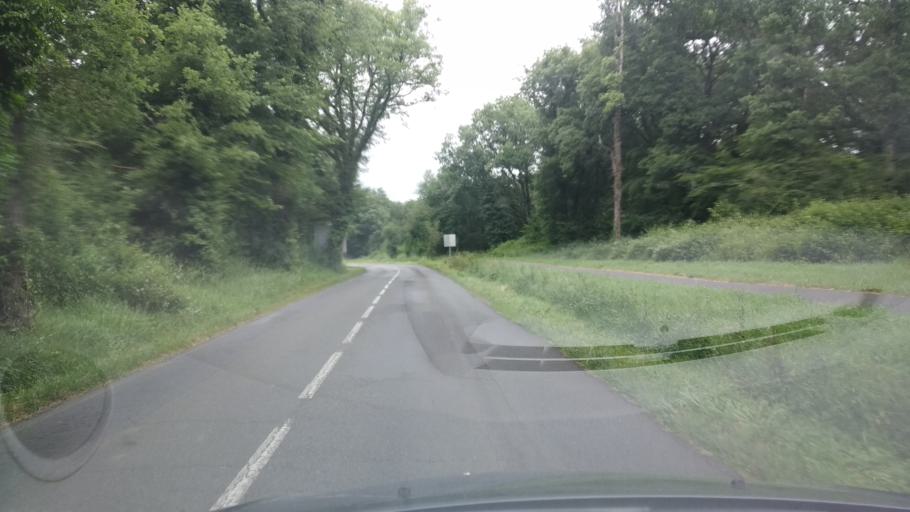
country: FR
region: Poitou-Charentes
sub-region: Departement de la Vienne
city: Vouneuil-sous-Biard
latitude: 46.5868
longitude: 0.2721
